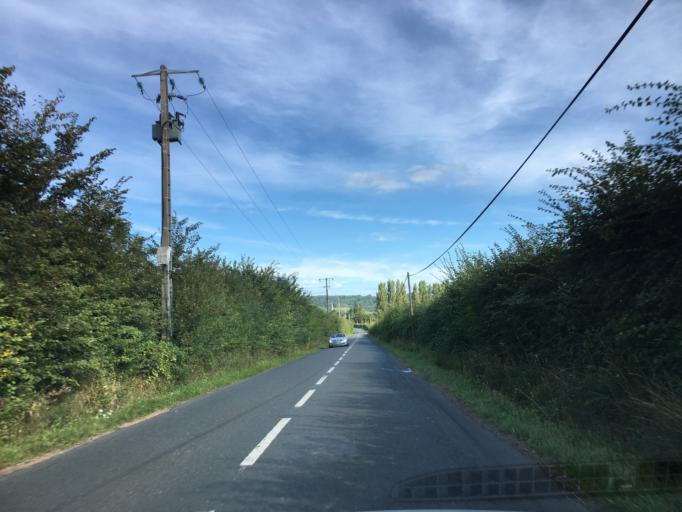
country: FR
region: Lower Normandy
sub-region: Departement du Calvados
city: Dozule
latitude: 49.1685
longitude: -0.0265
